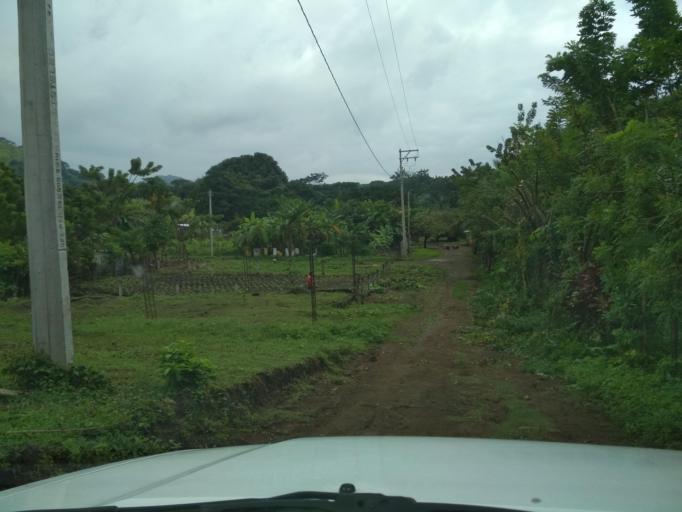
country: MX
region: Veracruz
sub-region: San Andres Tuxtla
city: Matacapan
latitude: 18.4359
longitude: -95.1500
